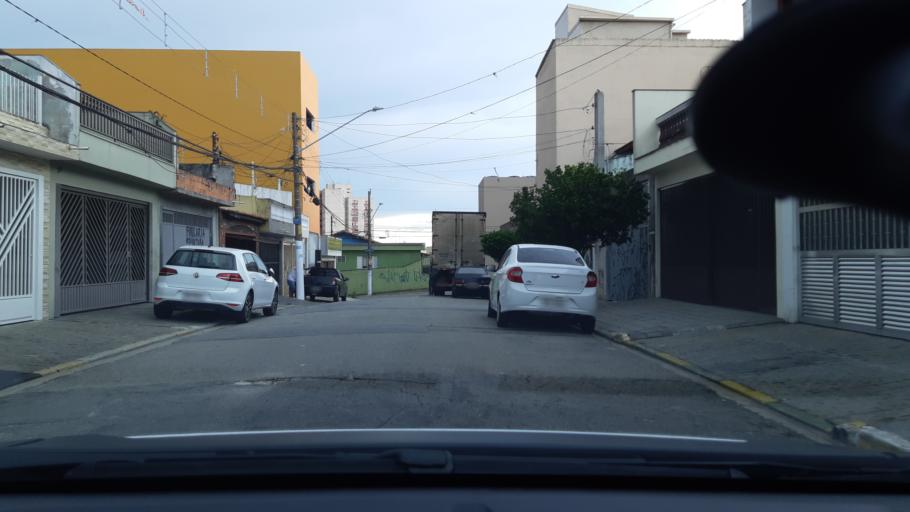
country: BR
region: Sao Paulo
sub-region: Sao Caetano Do Sul
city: Sao Caetano do Sul
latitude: -23.6043
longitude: -46.5211
